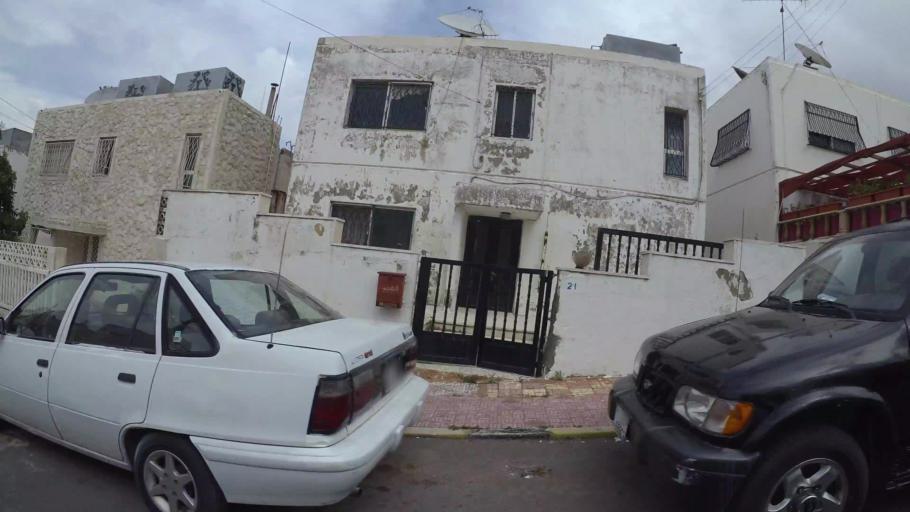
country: JO
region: Amman
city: Umm as Summaq
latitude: 31.8959
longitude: 35.8593
